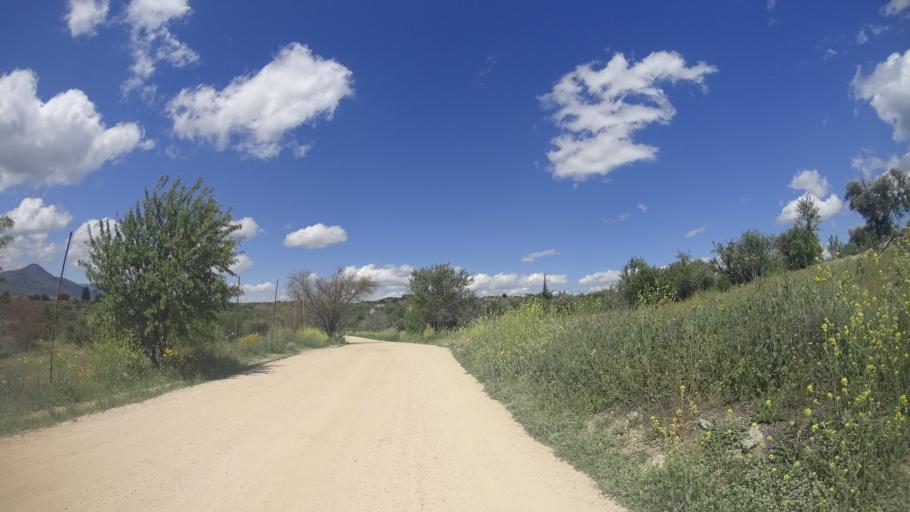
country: ES
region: Madrid
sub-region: Provincia de Madrid
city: San Martin de Valdeiglesias
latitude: 40.3653
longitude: -4.3864
